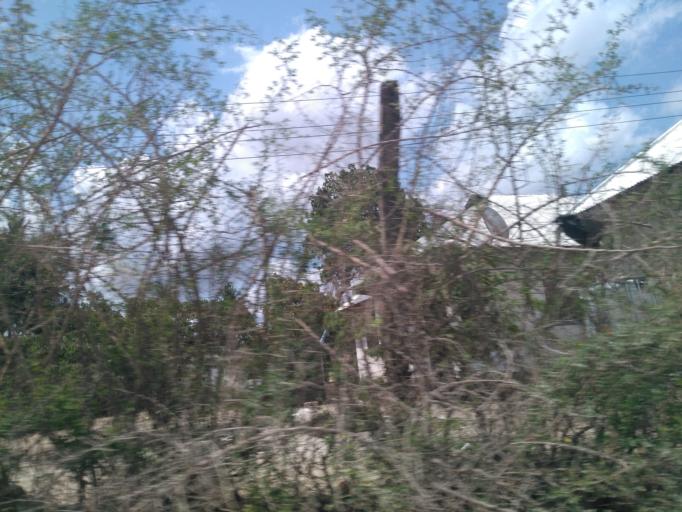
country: TZ
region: Dar es Salaam
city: Dar es Salaam
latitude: -6.8793
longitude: 39.3403
